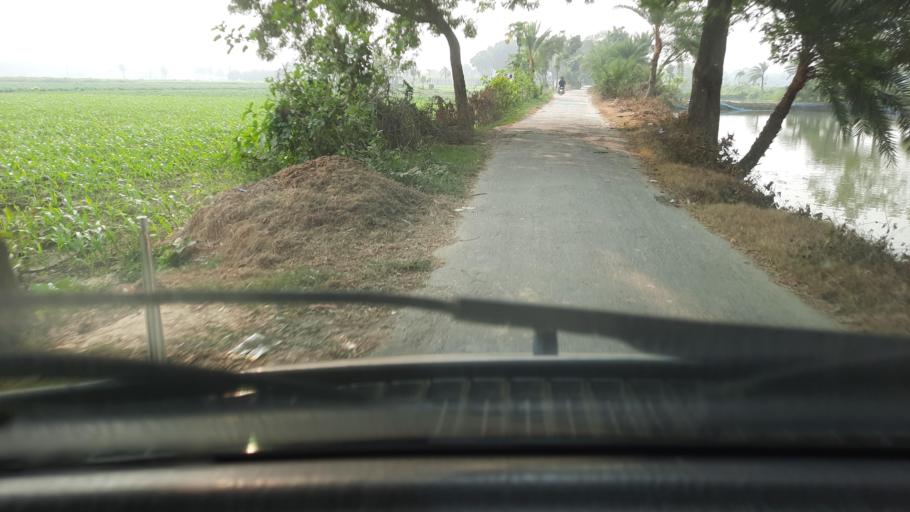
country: BD
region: Khulna
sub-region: Chuadanga
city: Nowlamary
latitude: 23.6007
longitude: 88.8516
